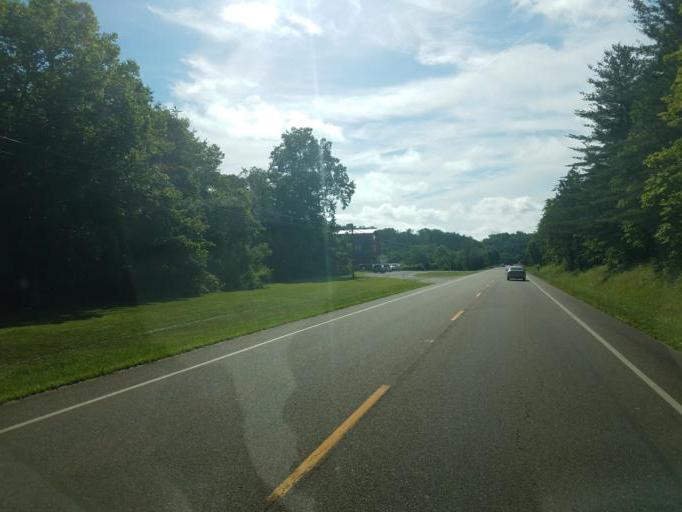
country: US
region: Ohio
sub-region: Gallia County
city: Gallipolis
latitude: 38.8596
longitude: -82.3409
